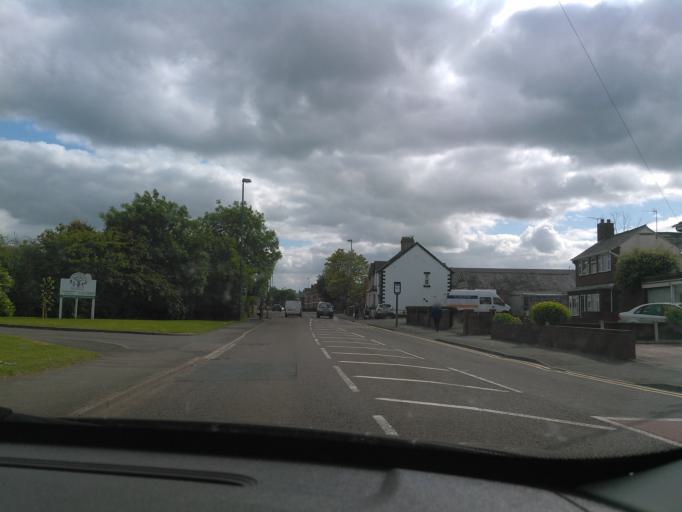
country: GB
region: England
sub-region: Shropshire
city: Shrewsbury
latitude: 52.7252
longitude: -2.7376
